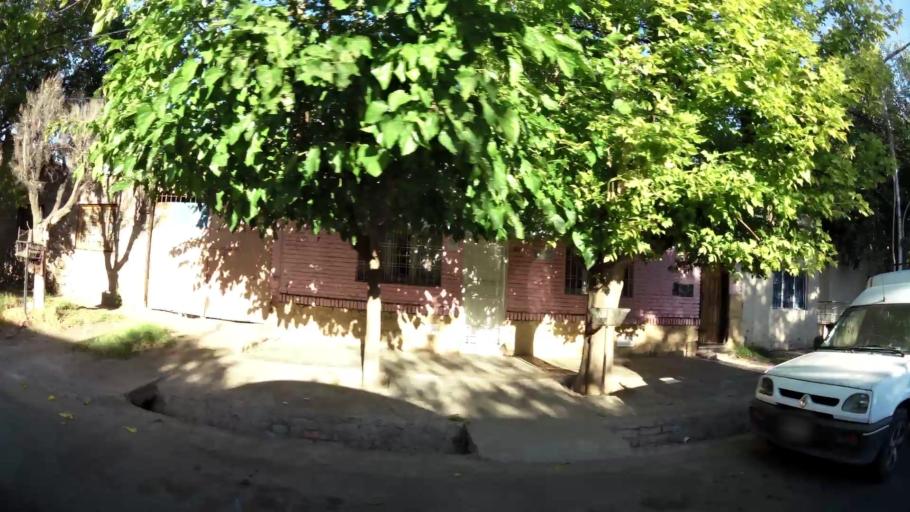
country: AR
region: Mendoza
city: Las Heras
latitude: -32.8644
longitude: -68.8259
